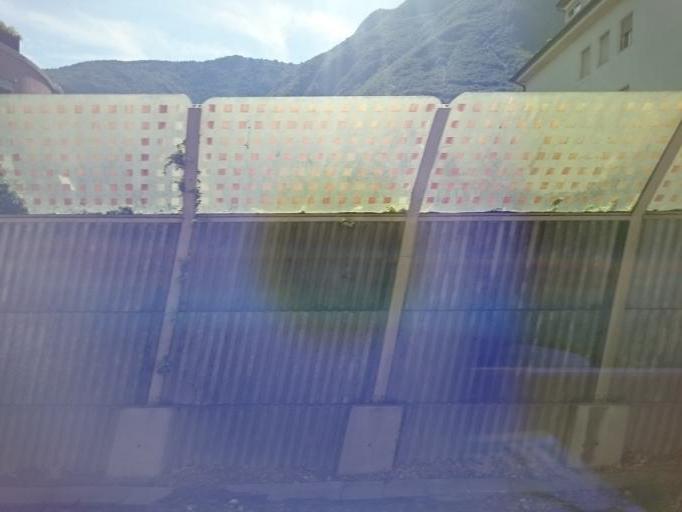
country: IT
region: Trentino-Alto Adige
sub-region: Bolzano
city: Bolzano
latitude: 46.4818
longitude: 11.3401
